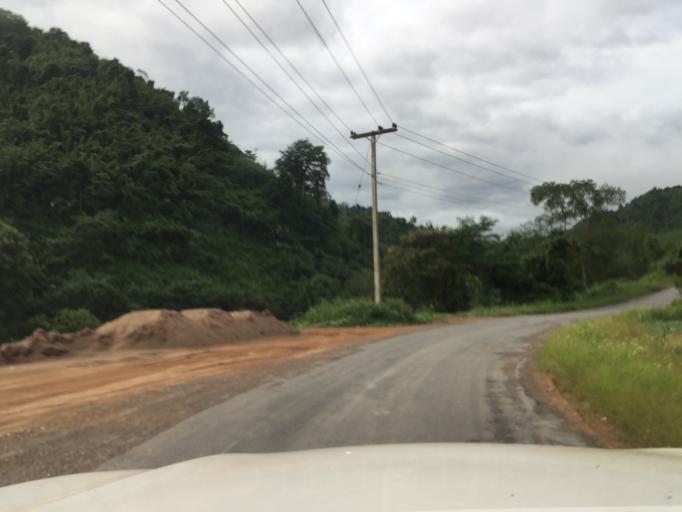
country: LA
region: Oudomxai
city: Muang La
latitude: 21.0703
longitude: 102.2417
